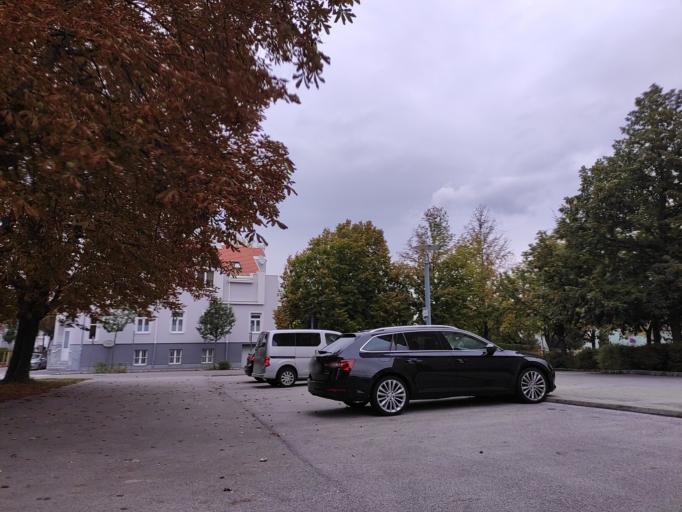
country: AT
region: Lower Austria
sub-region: Politischer Bezirk Baden
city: Baden
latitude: 48.0023
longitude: 16.2174
